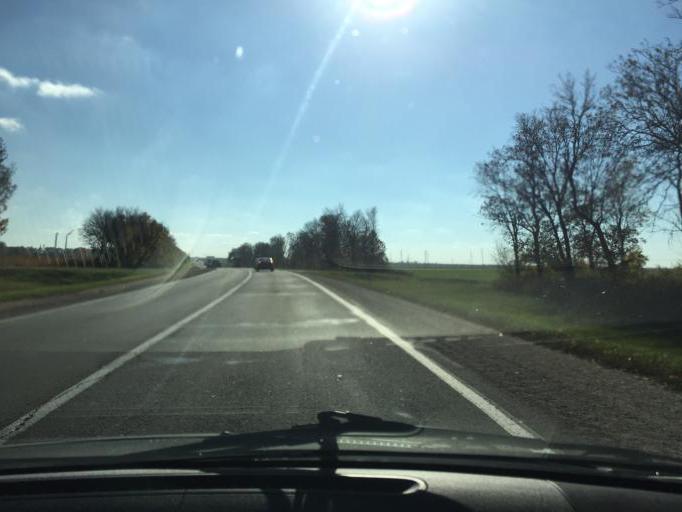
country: BY
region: Minsk
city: Salihorsk
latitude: 52.8787
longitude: 27.4677
